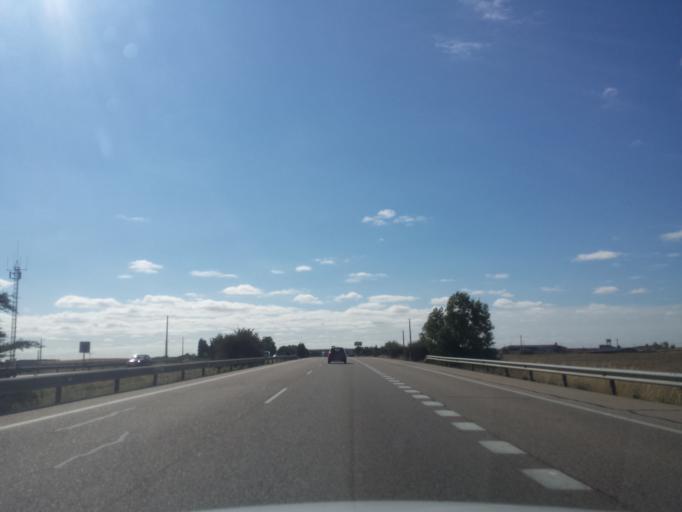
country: ES
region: Castille and Leon
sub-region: Provincia de Zamora
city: San Esteban del Molar
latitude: 41.9450
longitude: -5.5582
